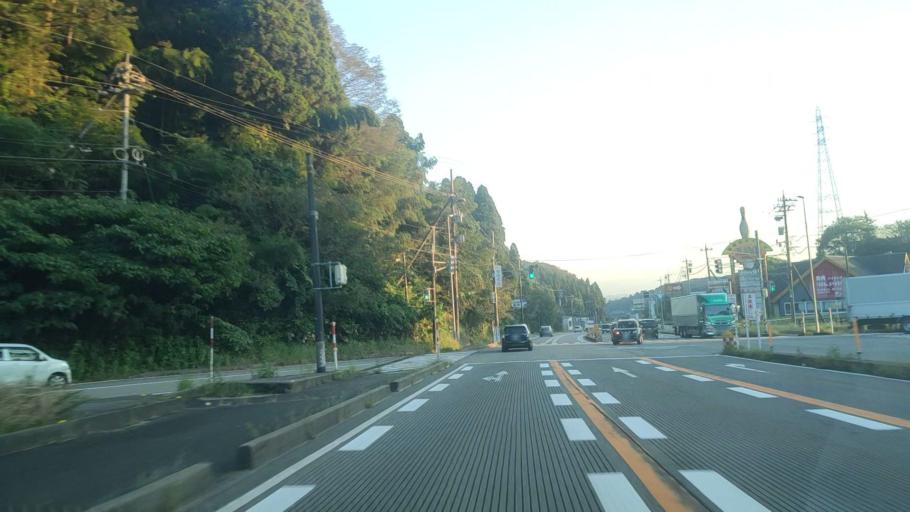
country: JP
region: Toyama
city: Takaoka
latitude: 36.7941
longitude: 137.0021
